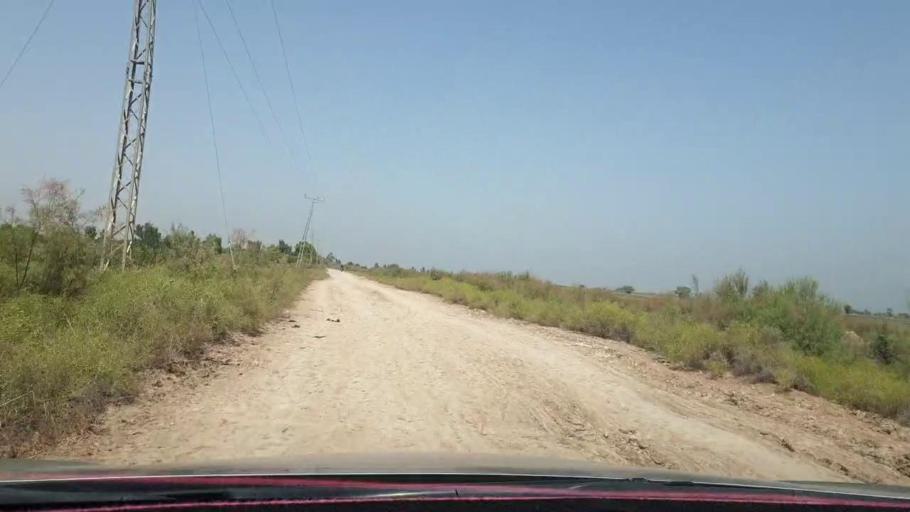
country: PK
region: Sindh
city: Warah
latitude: 27.4203
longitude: 67.6984
